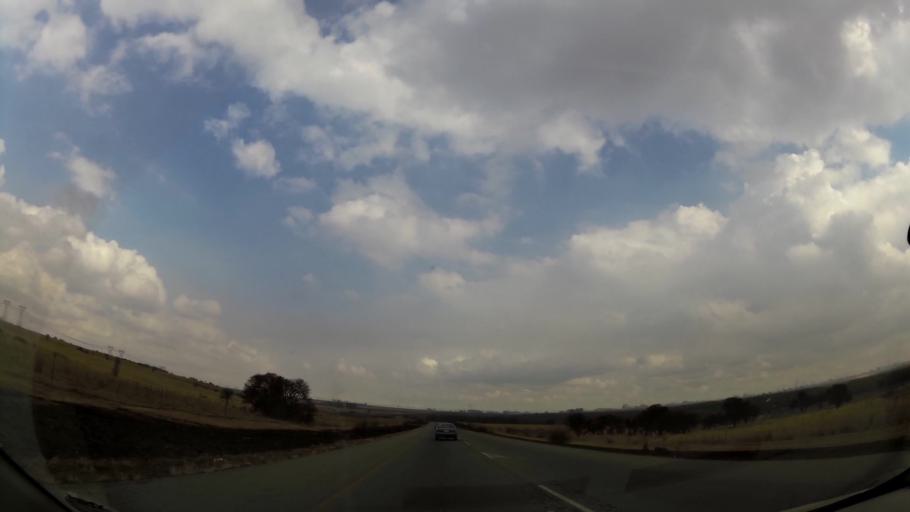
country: ZA
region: Orange Free State
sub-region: Fezile Dabi District Municipality
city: Sasolburg
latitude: -26.7979
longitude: 27.9148
